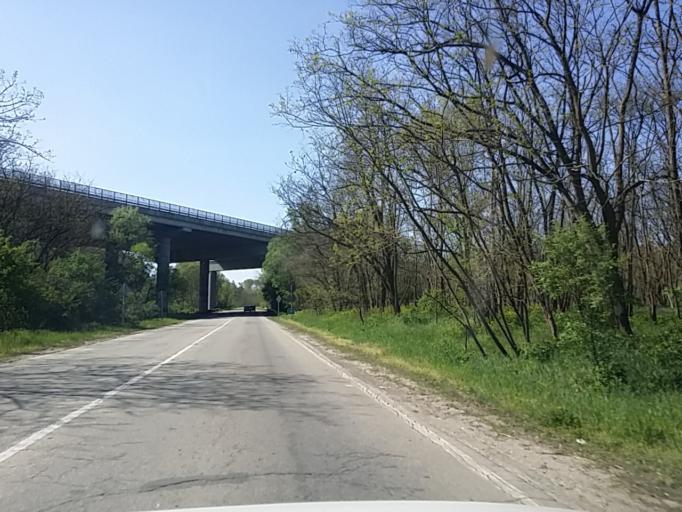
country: HU
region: Pest
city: Domony
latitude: 47.6232
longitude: 19.4124
